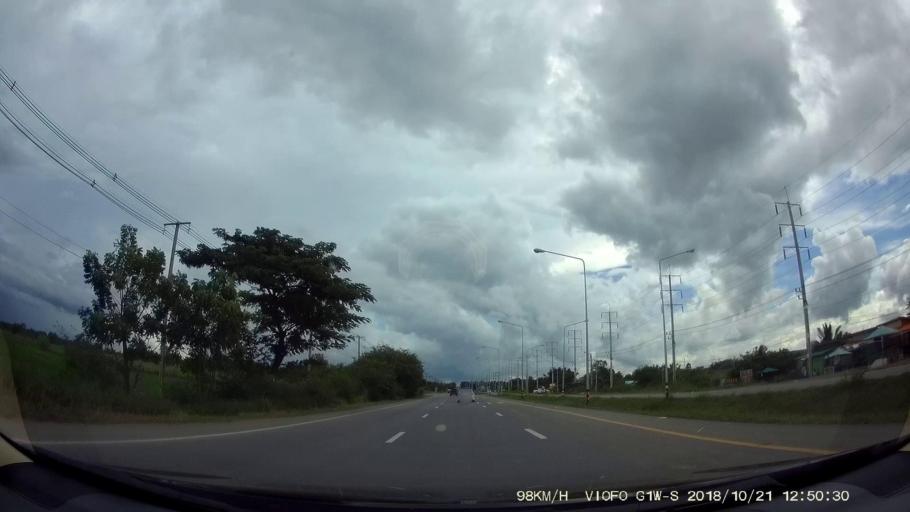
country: TH
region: Nakhon Ratchasima
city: Amphoe Sikhiu
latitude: 14.8812
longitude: 101.6905
